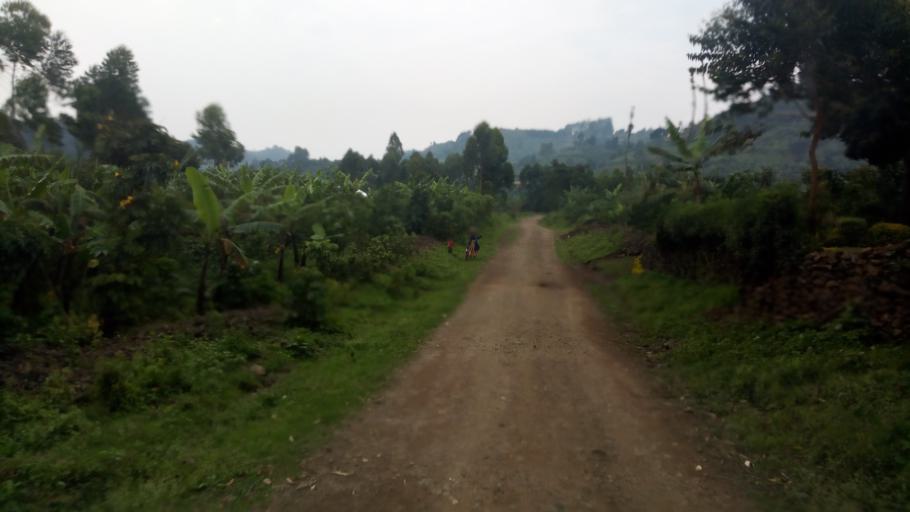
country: UG
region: Western Region
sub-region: Kisoro District
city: Kisoro
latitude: -1.2623
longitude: 29.6275
